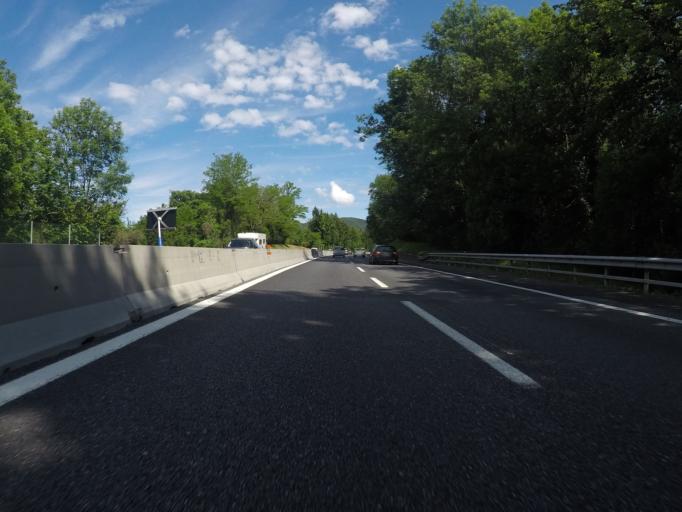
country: IT
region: Lombardy
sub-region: Provincia di Como
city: Lucino
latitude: 45.7905
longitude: 9.0486
